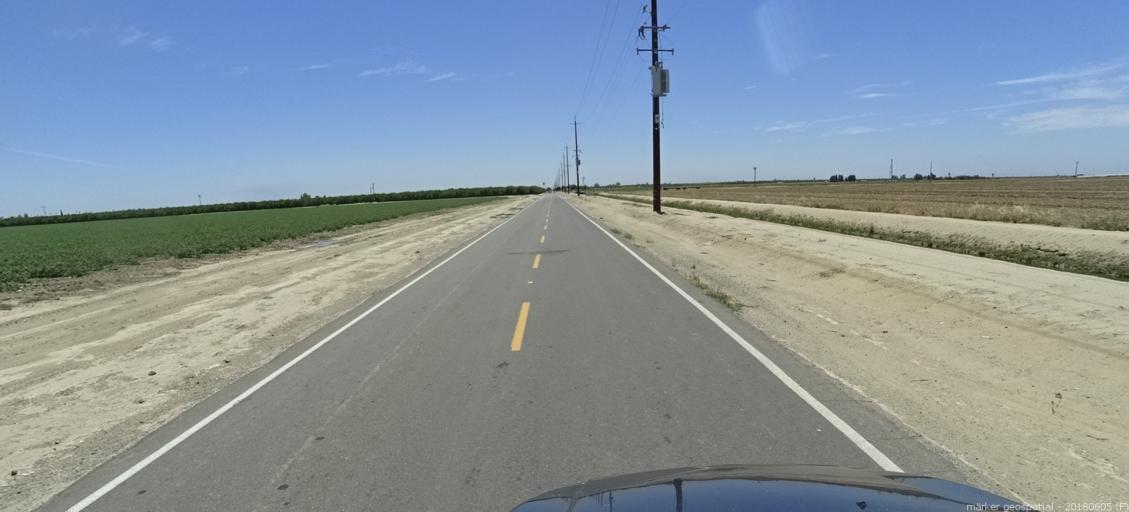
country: US
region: California
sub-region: Madera County
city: Chowchilla
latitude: 37.1008
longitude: -120.3109
